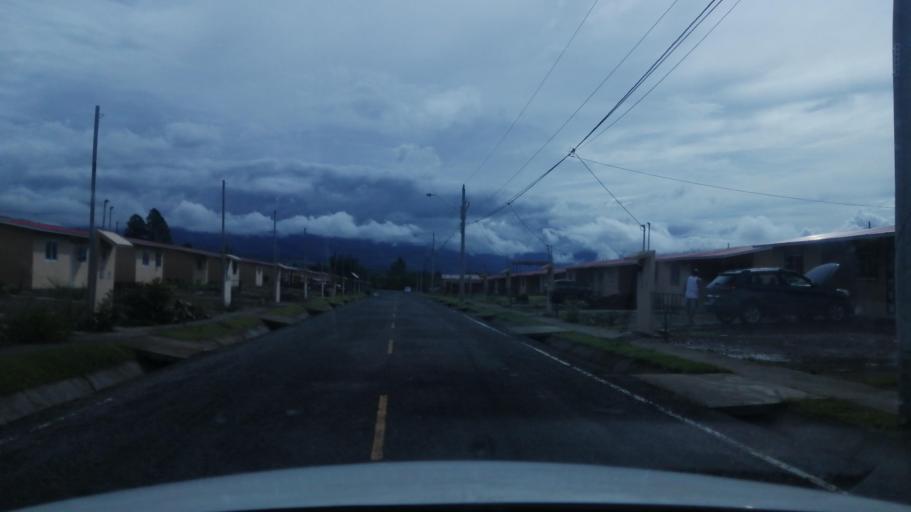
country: PA
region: Chiriqui
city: Potrerillos Abajo
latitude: 8.6660
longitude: -82.4293
